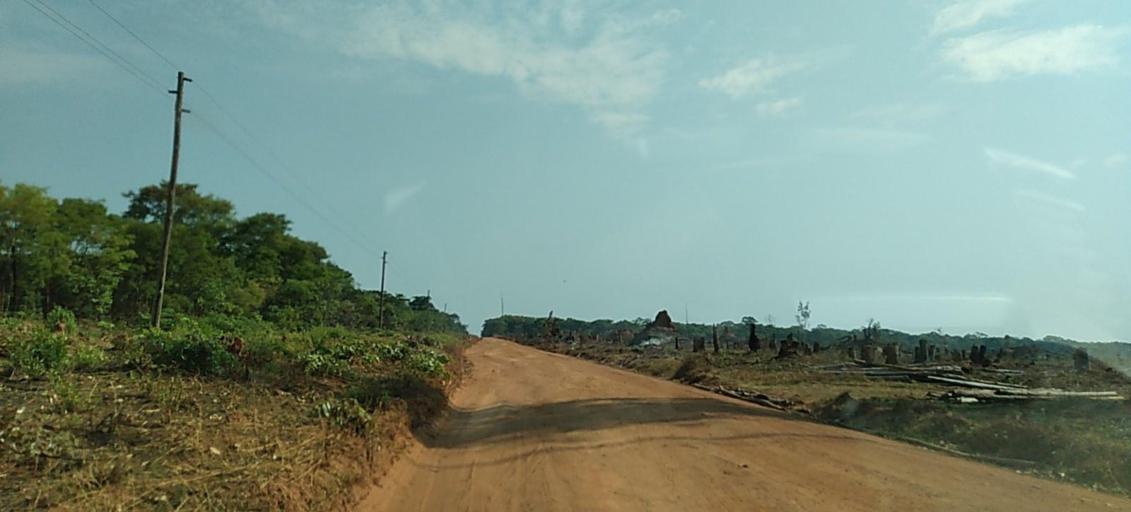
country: ZM
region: Copperbelt
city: Kalulushi
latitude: -12.9957
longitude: 27.8143
